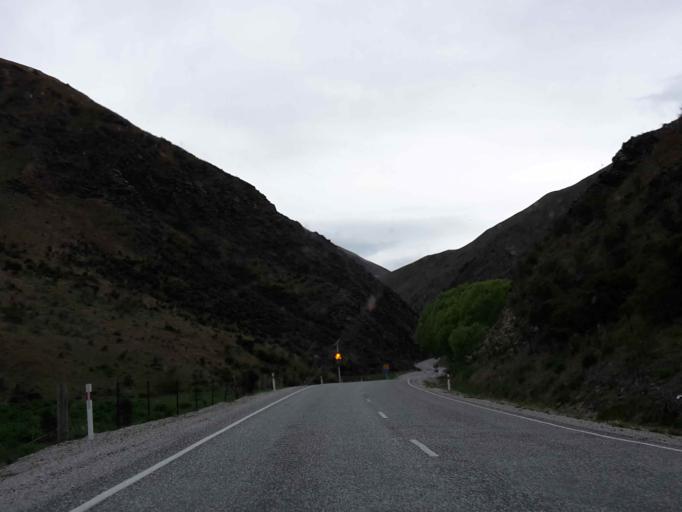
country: NZ
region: Otago
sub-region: Queenstown-Lakes District
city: Wanaka
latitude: -44.6000
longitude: 169.5554
